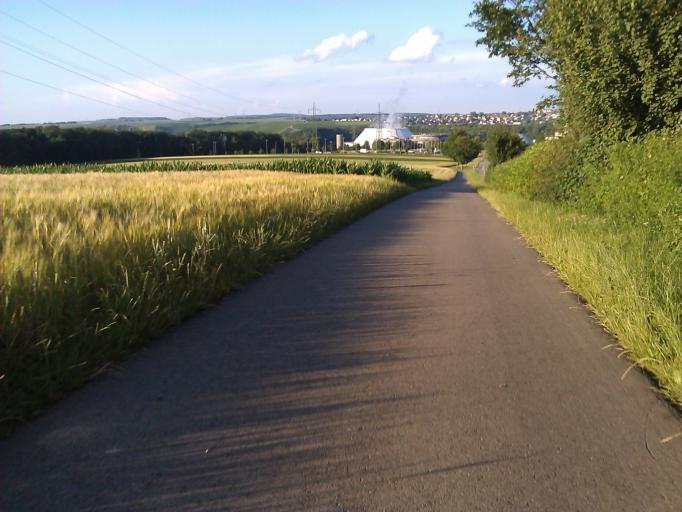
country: DE
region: Baden-Wuerttemberg
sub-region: Regierungsbezirk Stuttgart
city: Gemmrigheim
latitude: 49.0362
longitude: 9.1630
